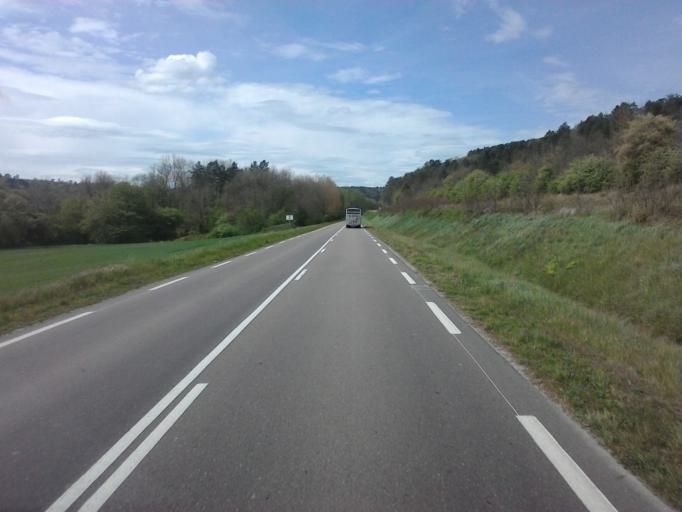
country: FR
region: Bourgogne
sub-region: Departement de l'Yonne
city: Vermenton
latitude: 47.6160
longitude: 3.7532
